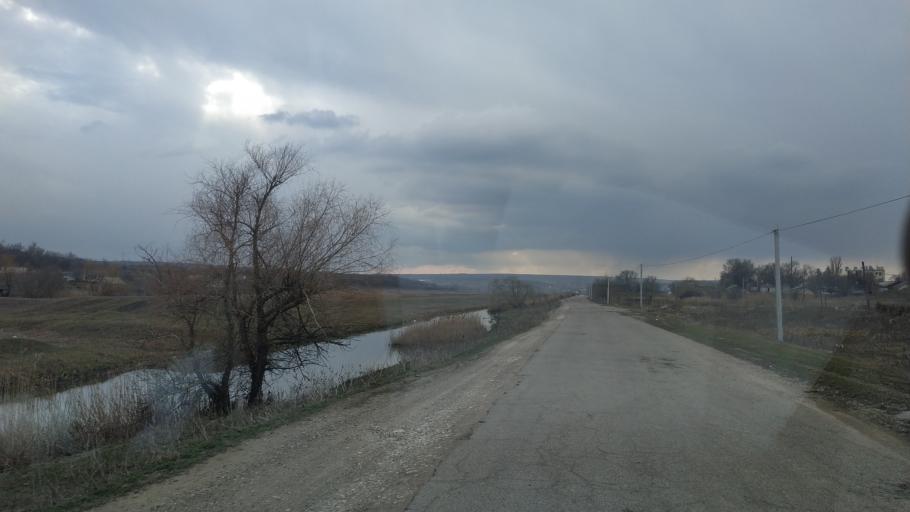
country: MD
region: Anenii Noi
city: Anenii Noi
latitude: 46.8903
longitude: 29.3003
